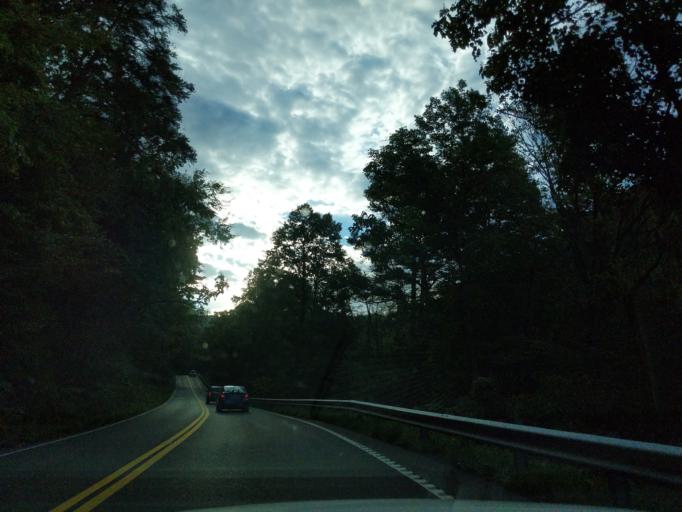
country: US
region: Tennessee
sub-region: Polk County
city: Benton
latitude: 35.1104
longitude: -84.5684
